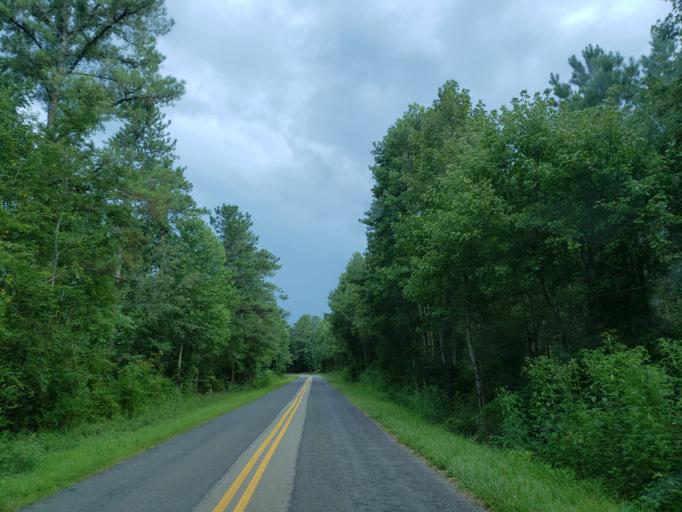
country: US
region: Georgia
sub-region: Pickens County
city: Jasper
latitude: 34.3917
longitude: -84.4660
